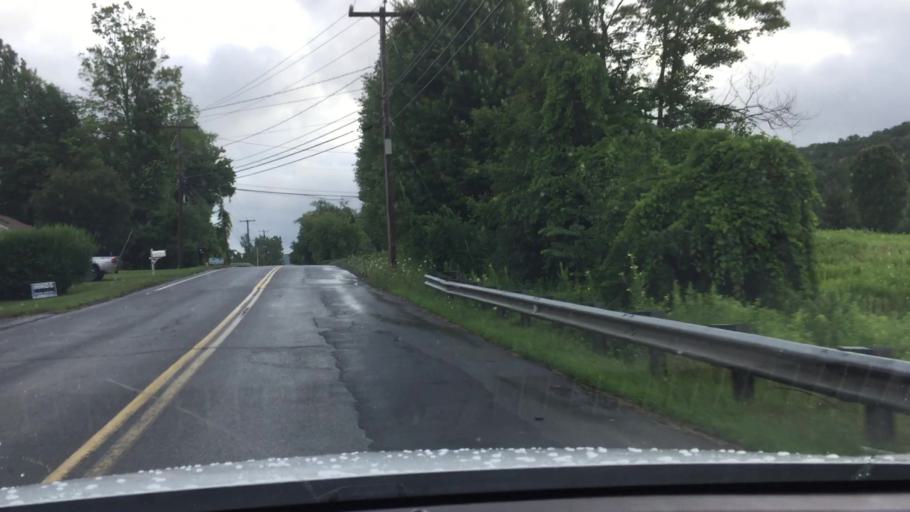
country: US
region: Massachusetts
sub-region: Berkshire County
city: Dalton
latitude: 42.4322
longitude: -73.1966
